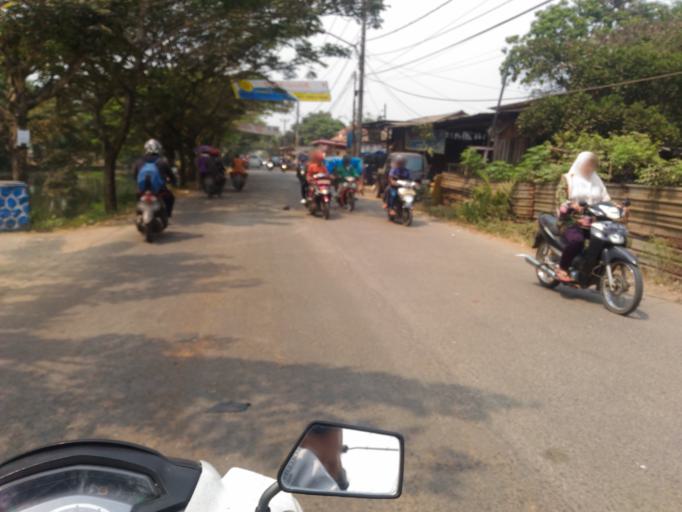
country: ID
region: West Java
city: Pasarkemis
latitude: -6.1413
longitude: 106.5465
